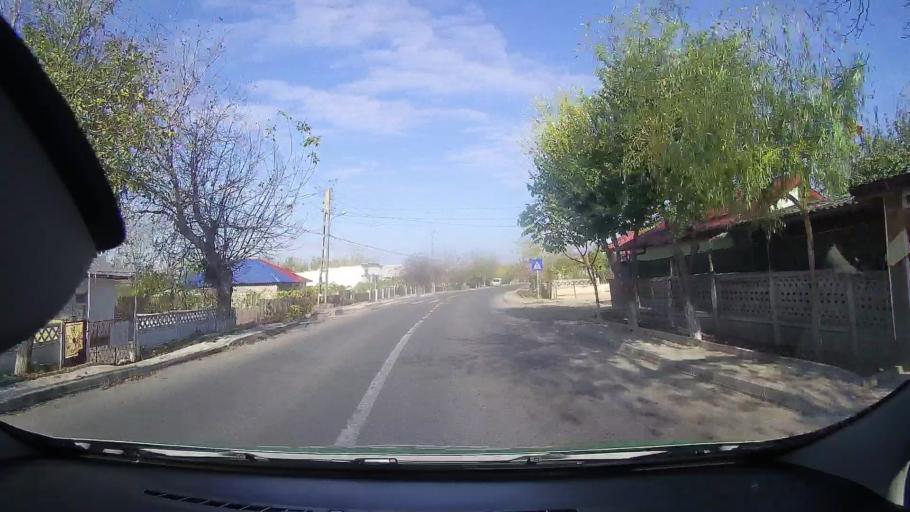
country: RO
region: Tulcea
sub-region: Comuna Valea Nucarilor
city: Valea Nucarilor
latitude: 45.0370
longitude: 28.9405
